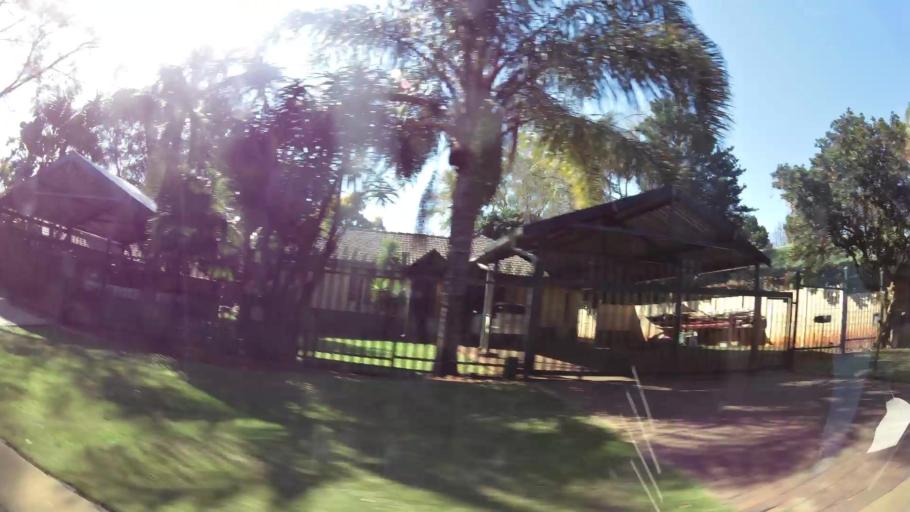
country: ZA
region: Gauteng
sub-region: City of Tshwane Metropolitan Municipality
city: Pretoria
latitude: -25.6827
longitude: 28.2330
